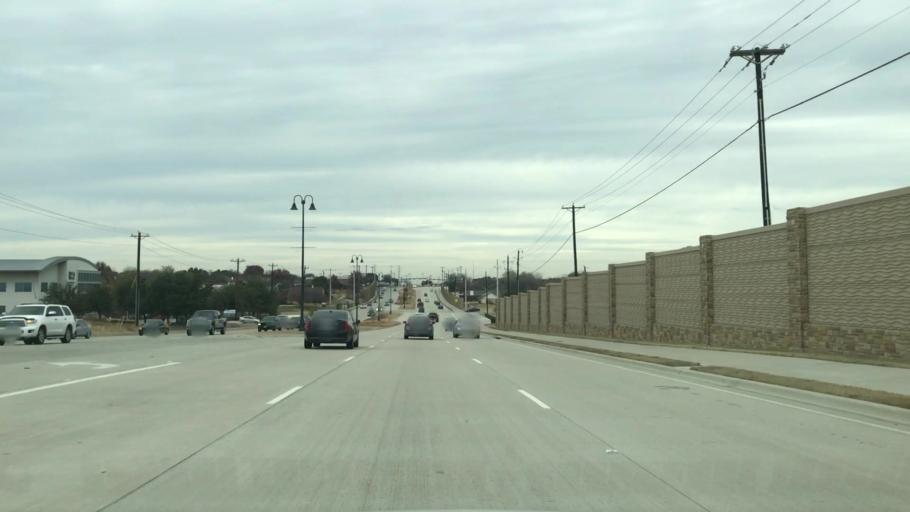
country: US
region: Texas
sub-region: Denton County
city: The Colony
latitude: 33.0899
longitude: -96.8927
